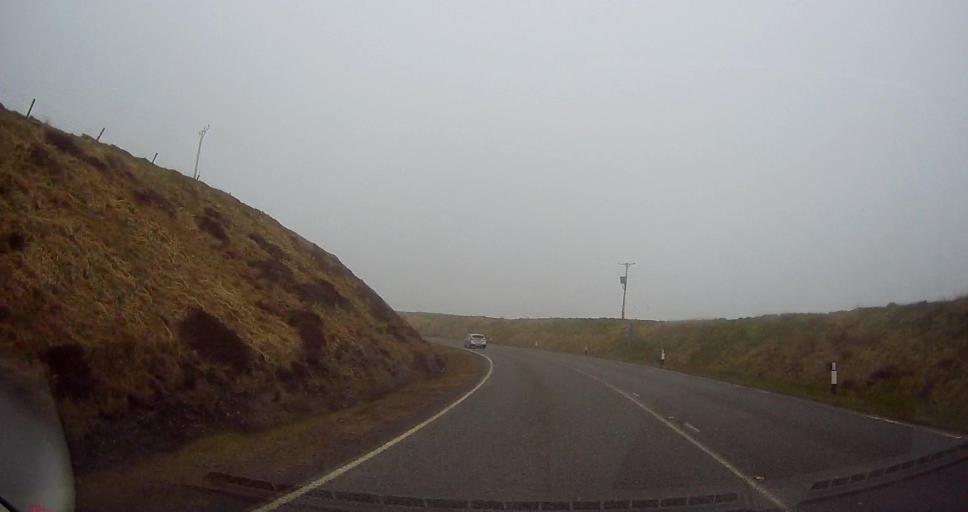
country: GB
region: Scotland
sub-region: Shetland Islands
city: Lerwick
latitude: 60.1378
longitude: -1.2324
